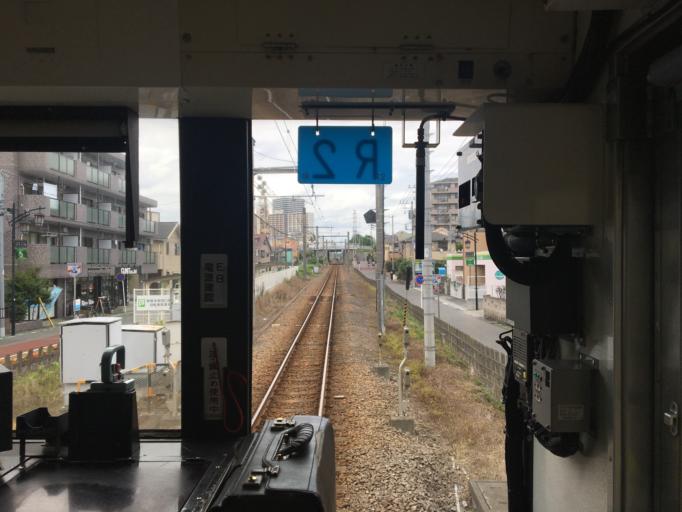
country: JP
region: Tokyo
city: Hachioji
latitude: 35.5815
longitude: 139.3526
